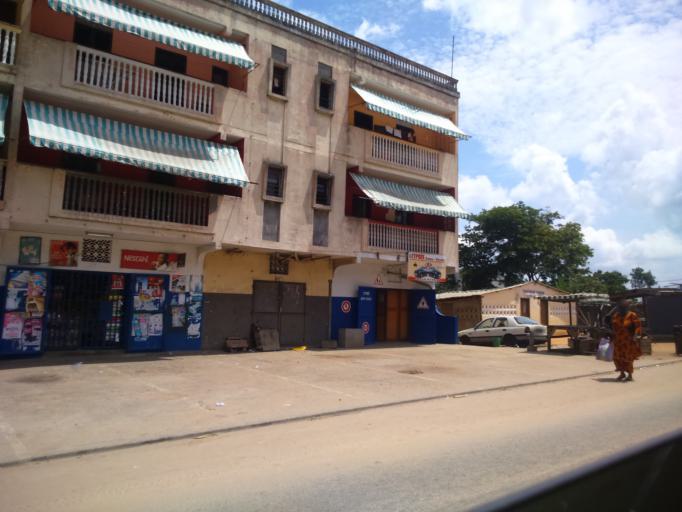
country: CI
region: Lagunes
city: Abidjan
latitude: 5.3388
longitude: -4.0922
